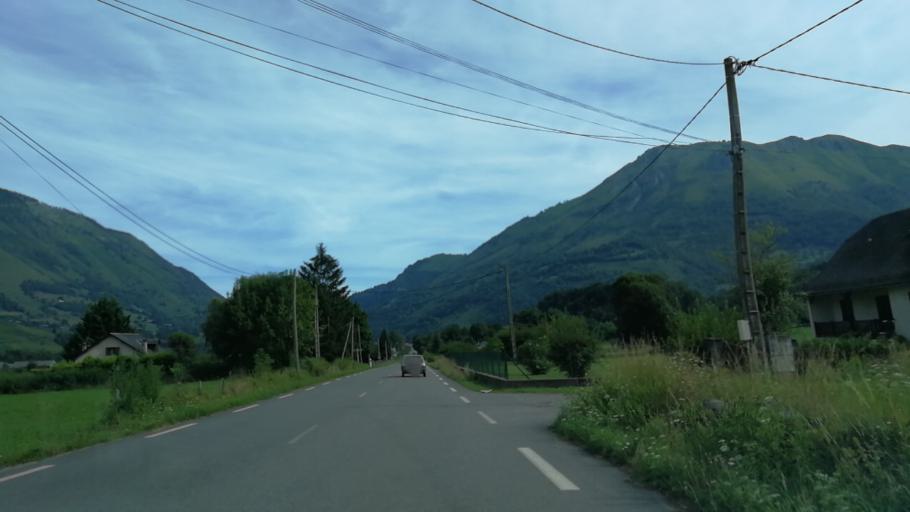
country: FR
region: Aquitaine
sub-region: Departement des Pyrenees-Atlantiques
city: Arette
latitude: 42.9805
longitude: -0.6057
